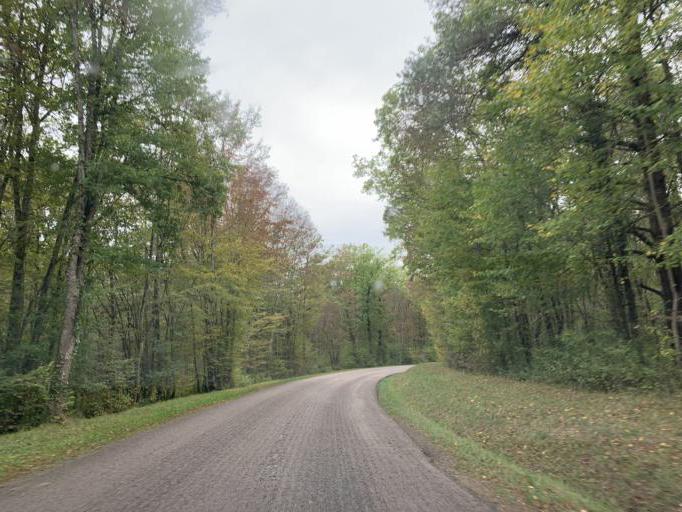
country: FR
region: Bourgogne
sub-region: Departement de l'Yonne
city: Vermenton
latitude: 47.5209
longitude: 3.7025
